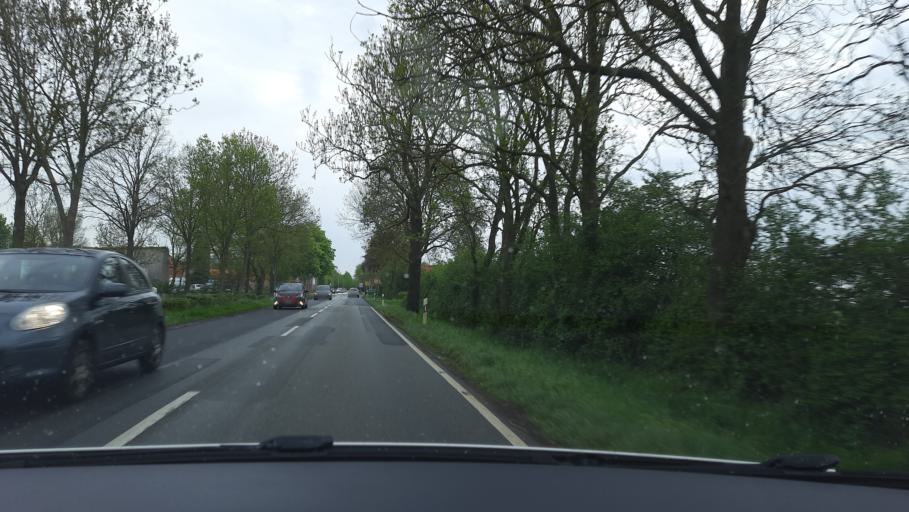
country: DE
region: Lower Saxony
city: Riede
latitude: 53.0020
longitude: 8.8947
